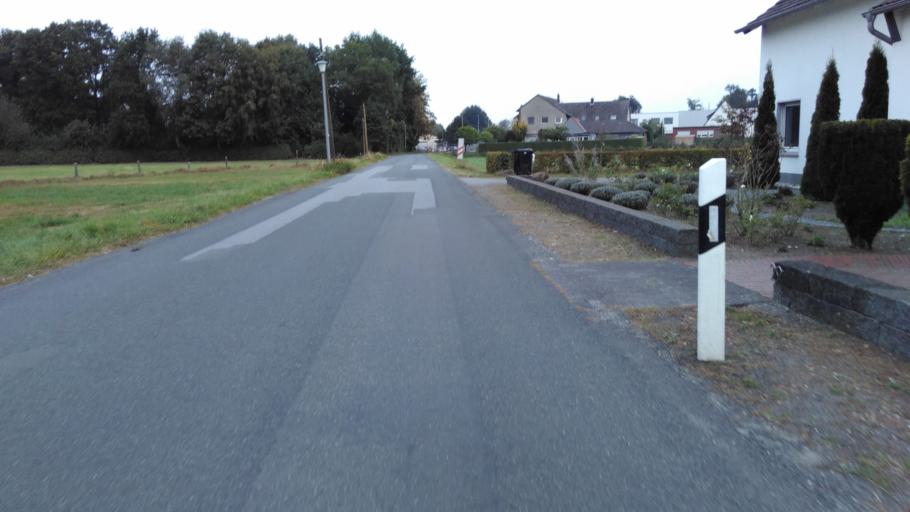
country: DE
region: North Rhine-Westphalia
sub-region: Regierungsbezirk Detmold
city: Verl
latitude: 51.8741
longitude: 8.4721
